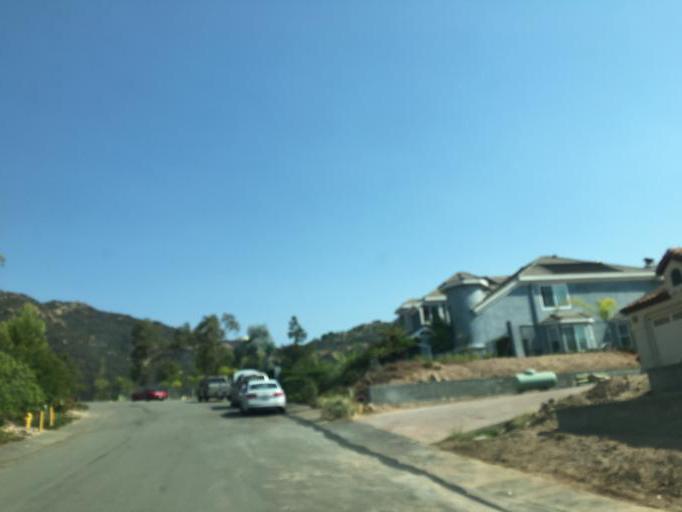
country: US
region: California
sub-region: Los Angeles County
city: Las Flores
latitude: 34.0674
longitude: -118.6511
